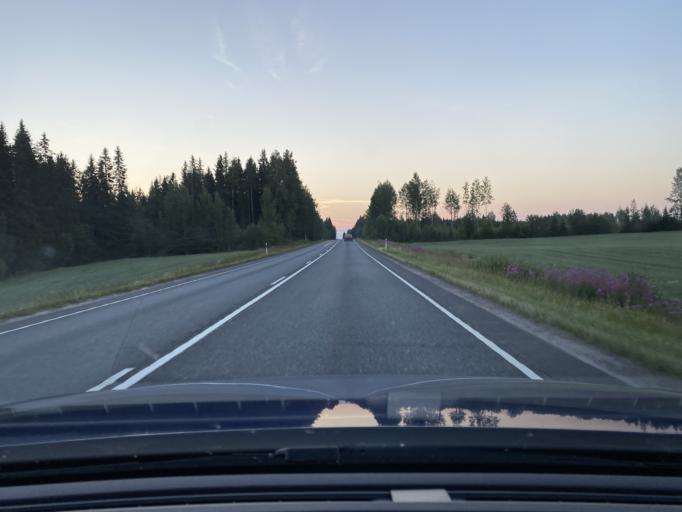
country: FI
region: Pirkanmaa
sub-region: Luoteis-Pirkanmaa
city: Ikaalinen
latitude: 61.8311
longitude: 22.9423
